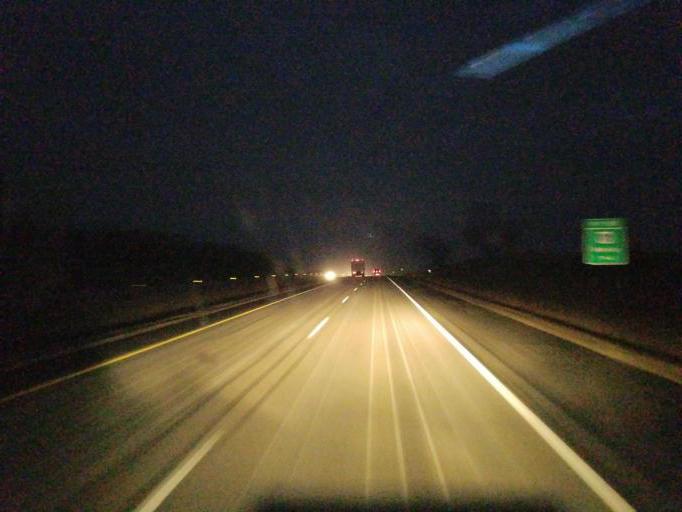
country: US
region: Iowa
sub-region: Guthrie County
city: Stuart
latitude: 41.4958
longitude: -94.4336
